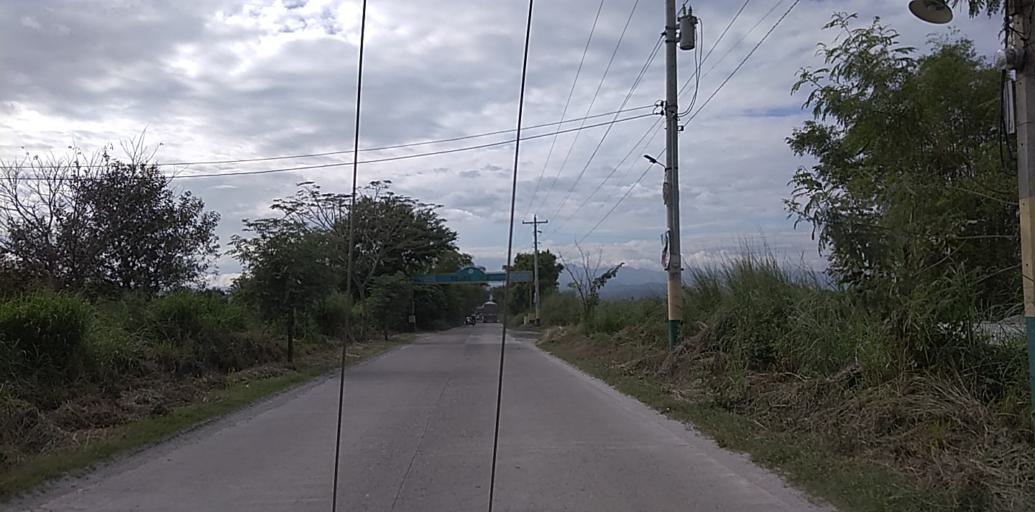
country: PH
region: Central Luzon
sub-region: Province of Pampanga
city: Porac
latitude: 15.0684
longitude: 120.5575
